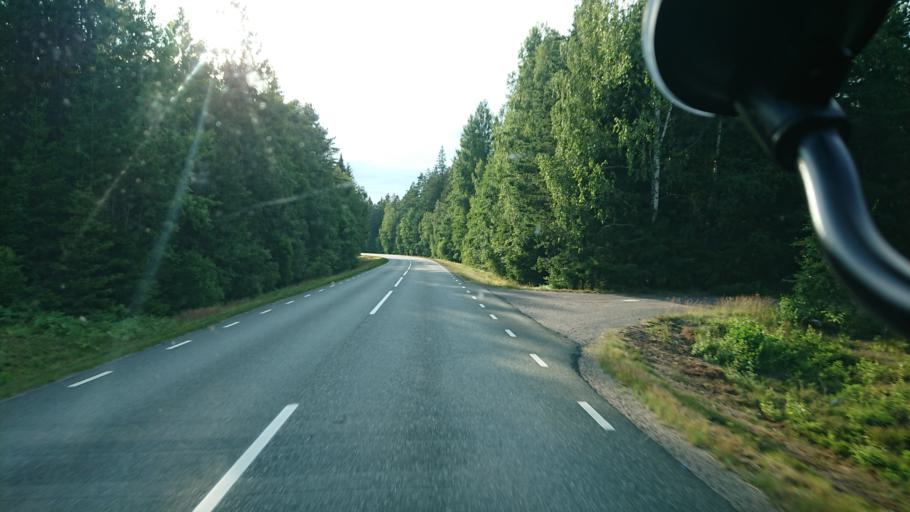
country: SE
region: Kronoberg
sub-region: Vaxjo Kommun
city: Rottne
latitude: 57.0364
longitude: 14.9220
